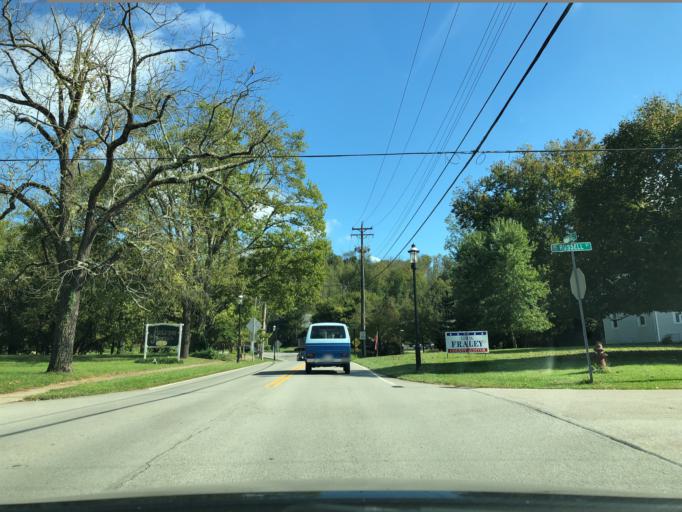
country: US
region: Ohio
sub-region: Hamilton County
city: The Village of Indian Hill
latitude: 39.2459
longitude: -84.2928
